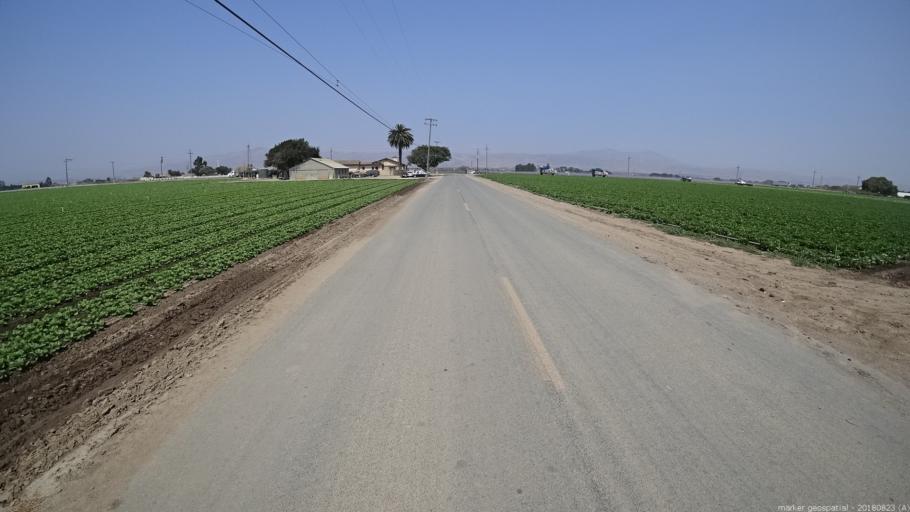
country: US
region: California
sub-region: Monterey County
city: Soledad
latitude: 36.4017
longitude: -121.3447
